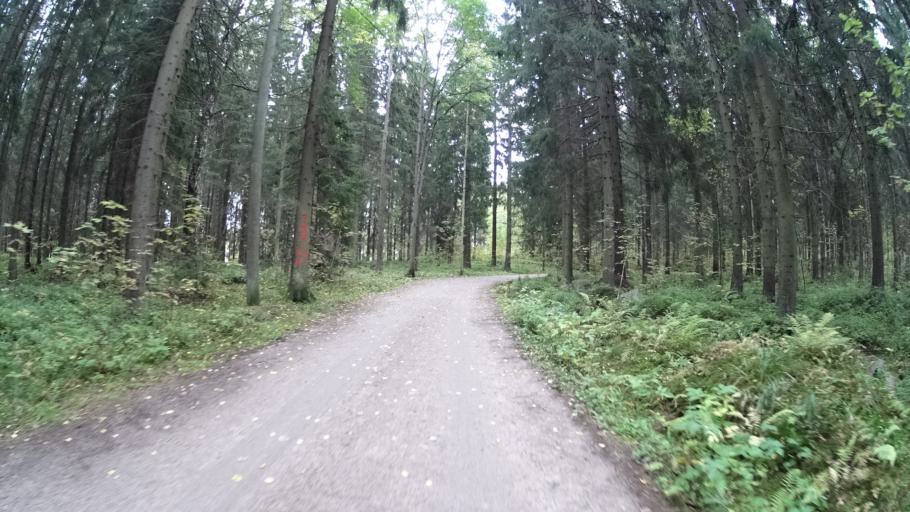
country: FI
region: Uusimaa
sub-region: Helsinki
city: Helsinki
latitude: 60.2494
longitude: 24.9144
